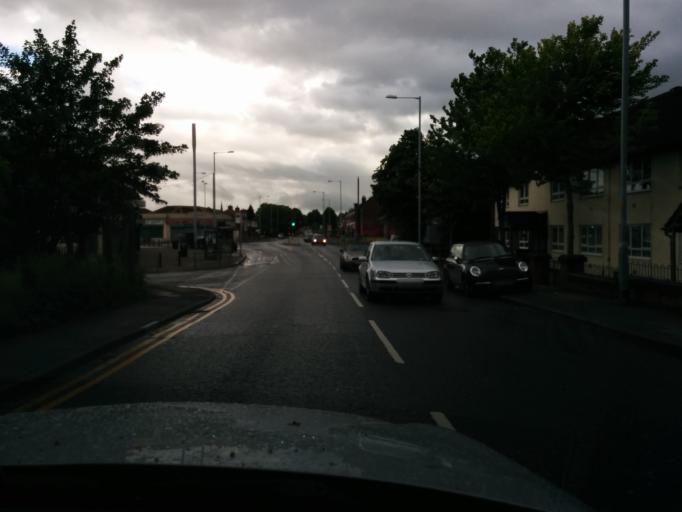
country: GB
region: England
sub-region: Borough of Stockport
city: Cheadle Hulme
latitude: 53.3881
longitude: -2.1705
